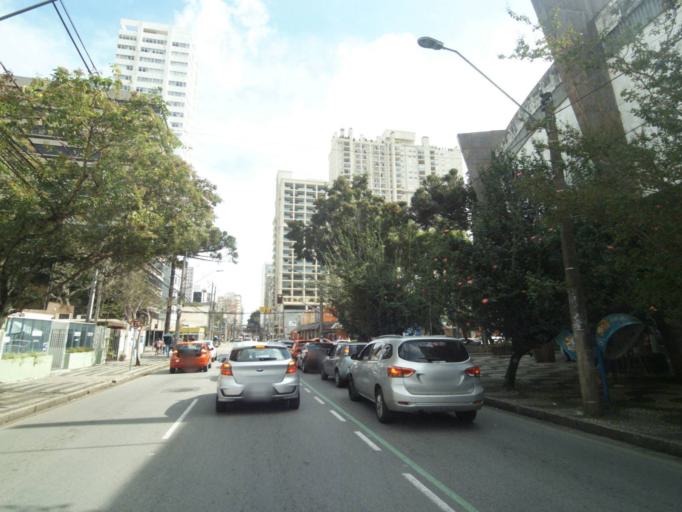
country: BR
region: Parana
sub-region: Curitiba
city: Curitiba
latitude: -25.4273
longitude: -49.2617
